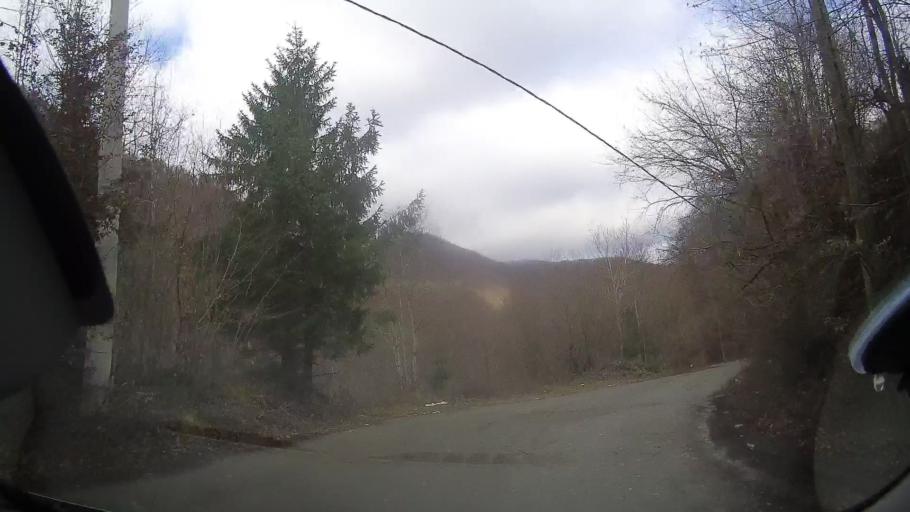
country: RO
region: Cluj
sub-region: Comuna Valea Ierii
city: Valea Ierii
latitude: 46.6857
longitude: 23.3063
